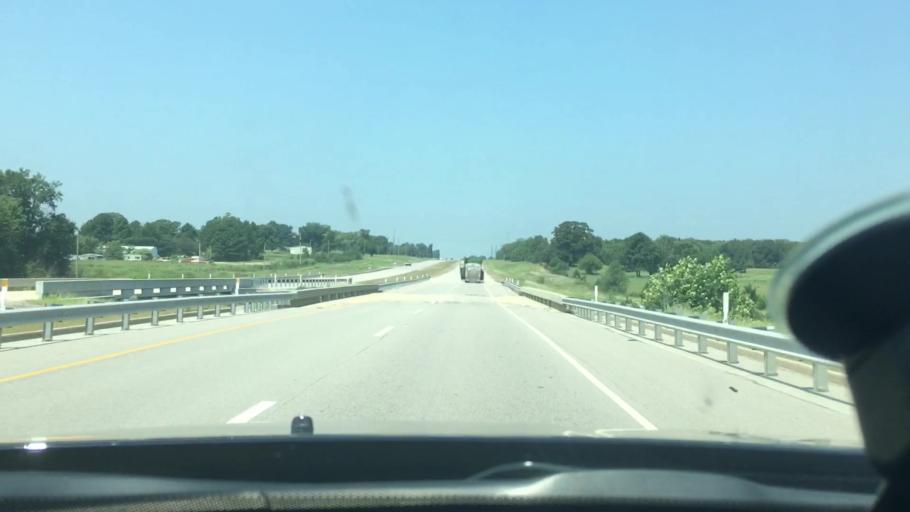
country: US
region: Oklahoma
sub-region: Atoka County
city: Atoka
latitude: 34.3236
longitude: -96.0406
